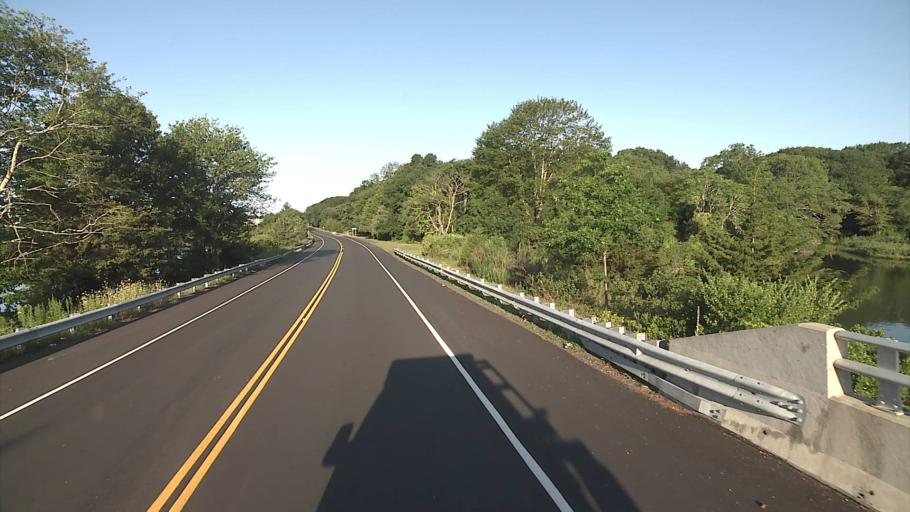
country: US
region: Connecticut
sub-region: New London County
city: Mystic
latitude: 41.3506
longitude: -71.9062
